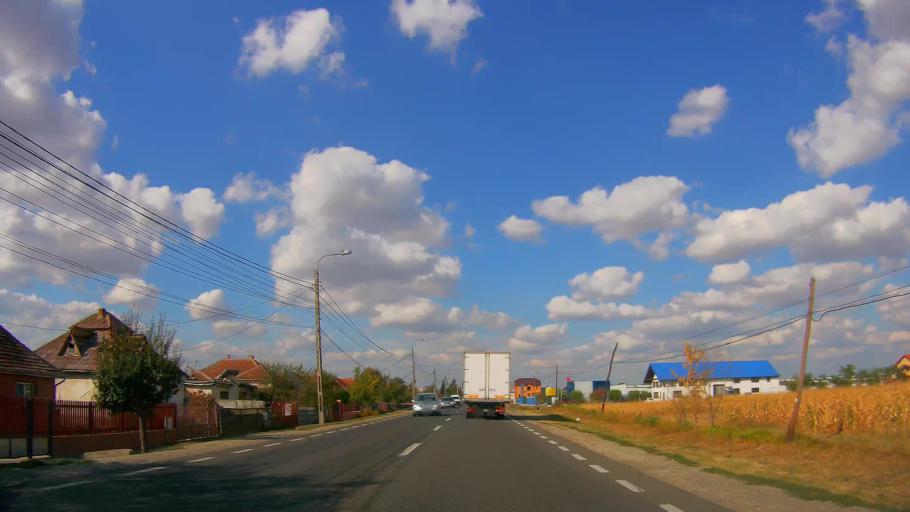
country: RO
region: Satu Mare
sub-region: Comuna Paulesti
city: Paulesti
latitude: 47.7496
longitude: 22.8832
